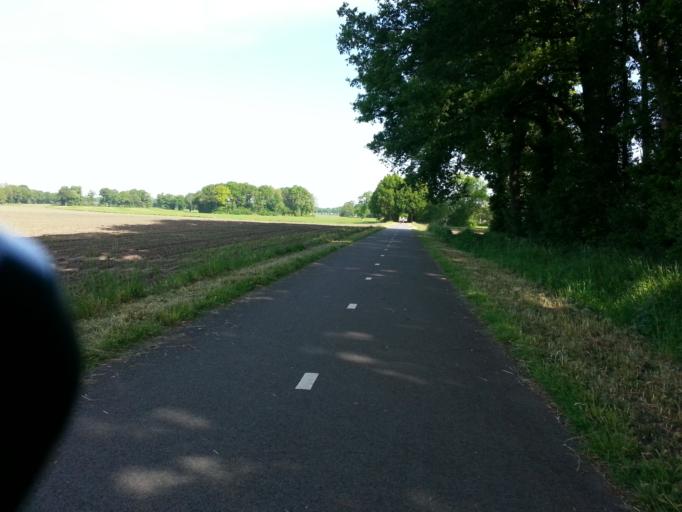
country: NL
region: Gelderland
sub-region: Berkelland
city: Eibergen
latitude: 52.1085
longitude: 6.6387
